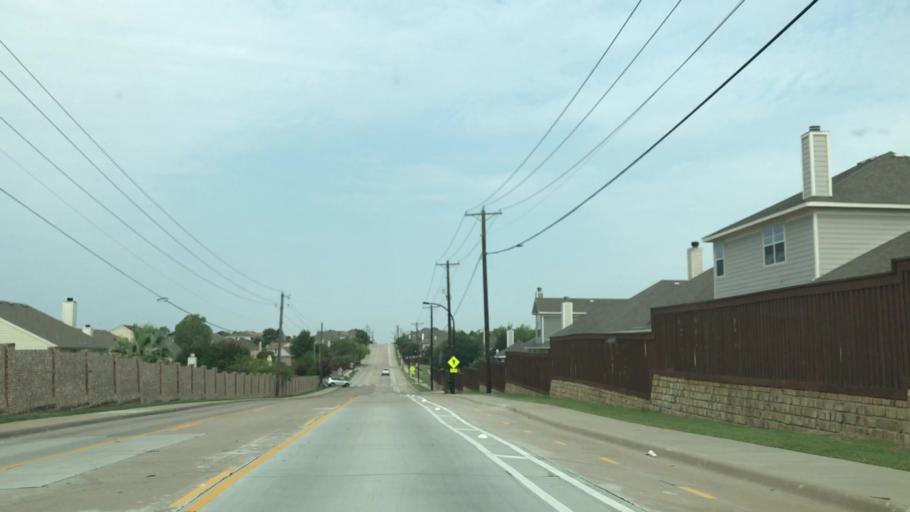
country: US
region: Texas
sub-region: Tarrant County
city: Keller
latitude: 32.9020
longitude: -97.2753
